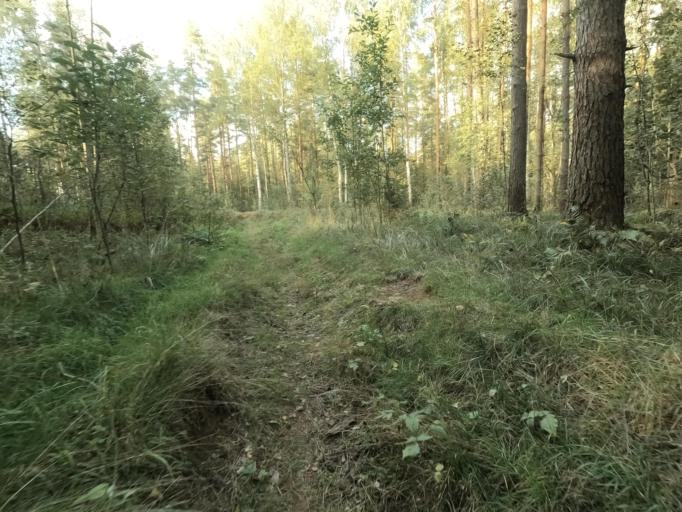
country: RU
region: Leningrad
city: Imeni Sverdlova
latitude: 59.8493
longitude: 30.7282
